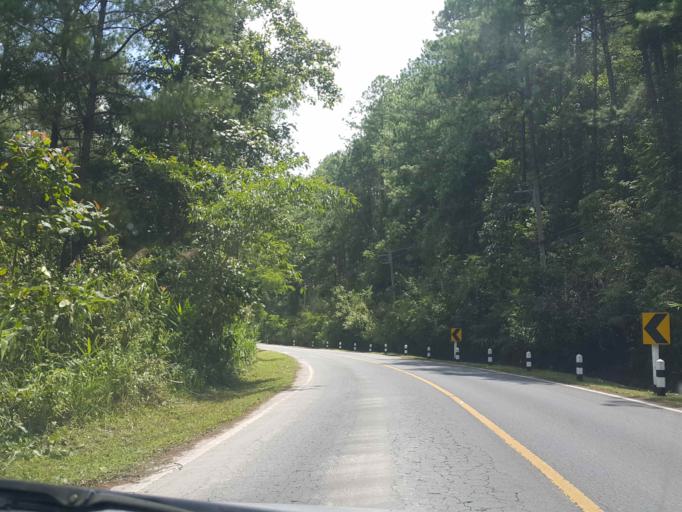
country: TH
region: Chiang Mai
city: Chom Thong
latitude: 18.5425
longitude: 98.5767
